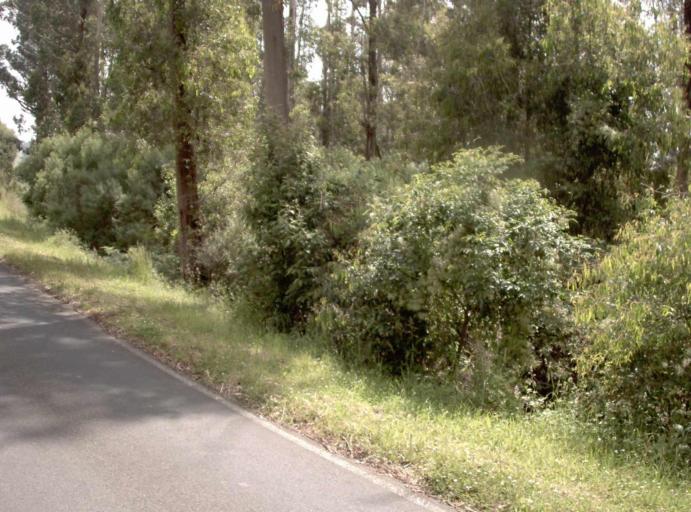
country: AU
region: Victoria
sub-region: Latrobe
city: Traralgon
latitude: -38.3437
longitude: 146.5715
